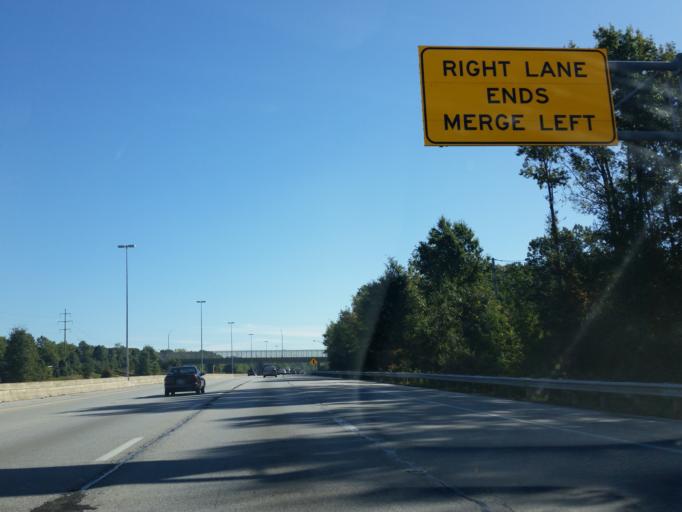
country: US
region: Ohio
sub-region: Cuyahoga County
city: Bay Village
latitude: 41.4754
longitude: -81.8864
